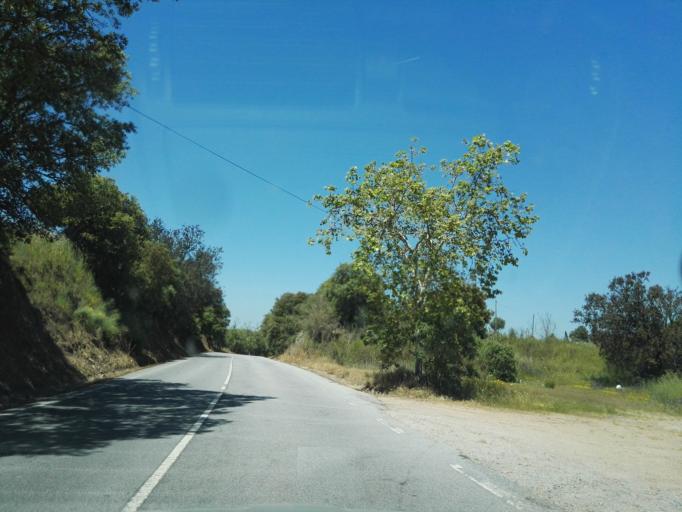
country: PT
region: Portalegre
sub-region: Elvas
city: Elvas
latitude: 38.9880
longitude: -7.2390
